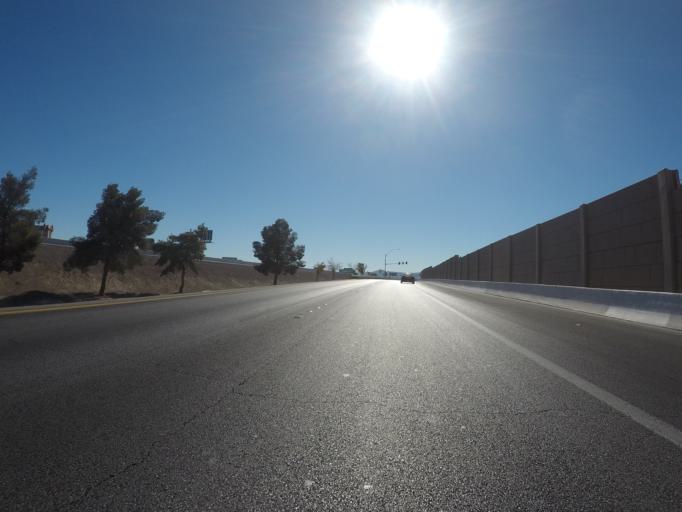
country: US
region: Nevada
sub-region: Clark County
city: Winchester
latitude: 36.1355
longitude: -115.0910
